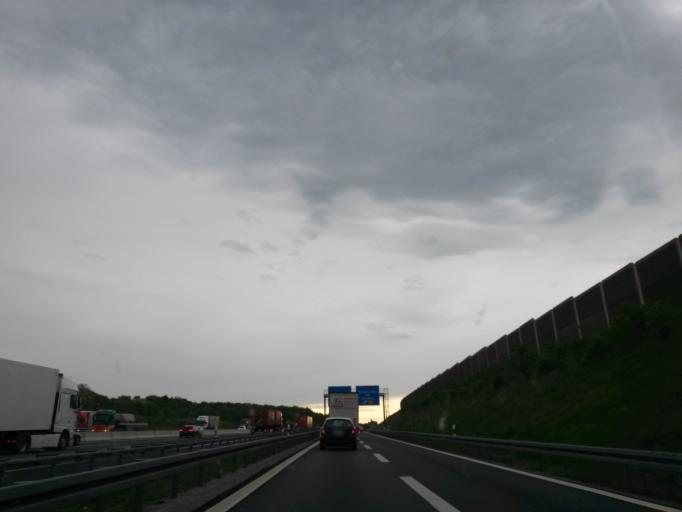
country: DE
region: Bavaria
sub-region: Regierungsbezirk Unterfranken
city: Kist
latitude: 49.7491
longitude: 9.8381
